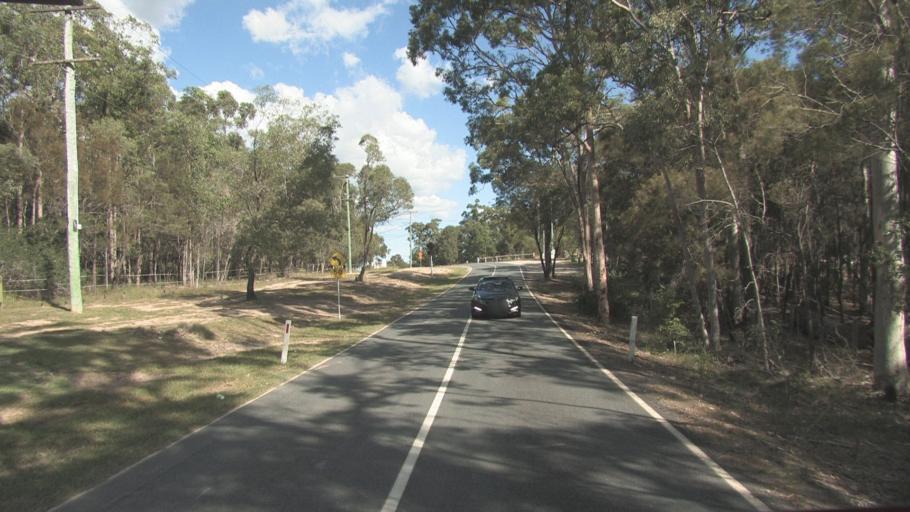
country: AU
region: Queensland
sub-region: Logan
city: Slacks Creek
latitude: -27.6429
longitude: 153.2065
